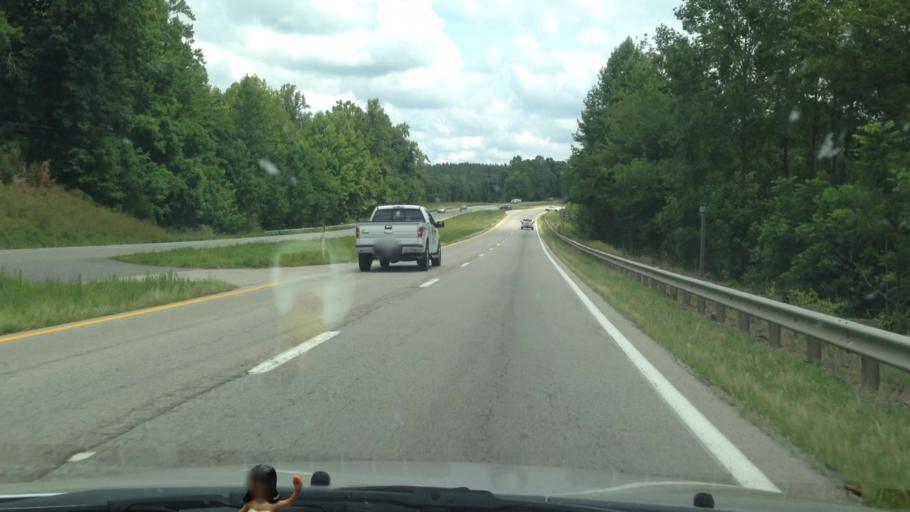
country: US
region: Virginia
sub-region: Pittsylvania County
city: Gretna
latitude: 36.9099
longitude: -79.3880
